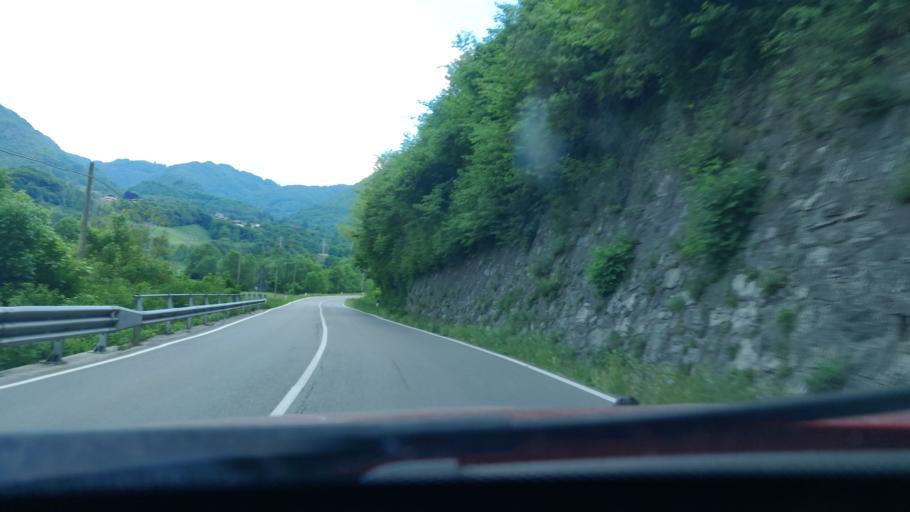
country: IT
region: Lombardy
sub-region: Provincia di Lecco
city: Pasturo
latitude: 45.9397
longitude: 9.4521
